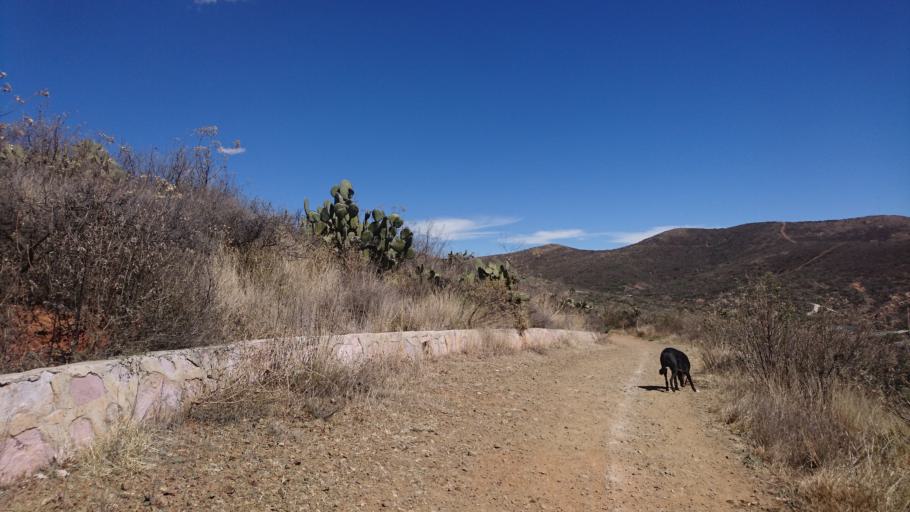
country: MX
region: Zacatecas
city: Zacatecas
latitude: 22.7809
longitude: -102.5468
